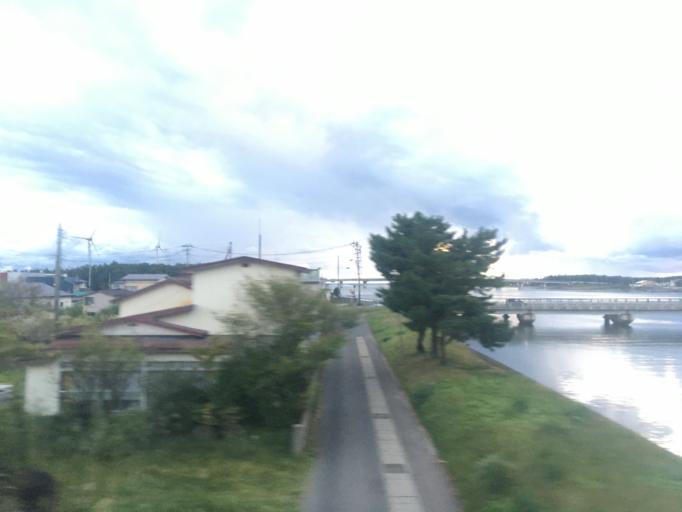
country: JP
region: Akita
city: Tenno
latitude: 39.9009
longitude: 139.9593
